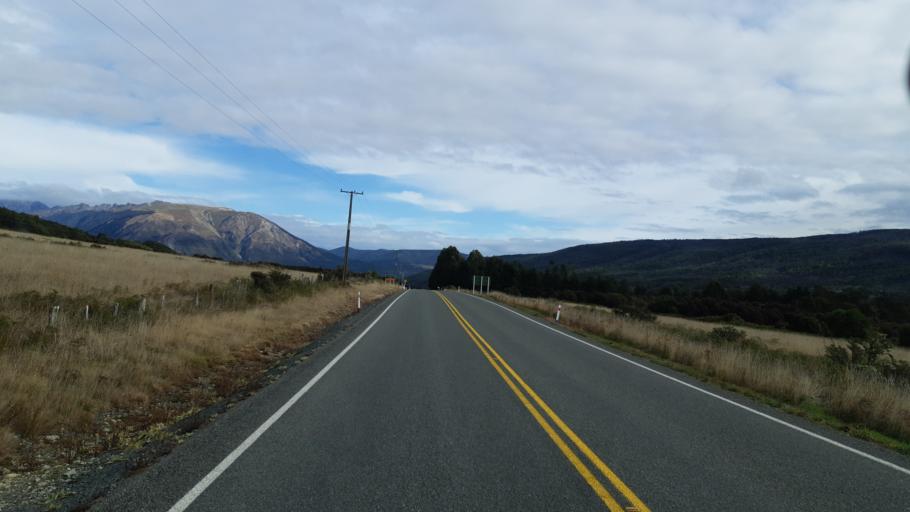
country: NZ
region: Tasman
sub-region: Tasman District
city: Wakefield
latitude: -41.7838
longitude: 172.8987
